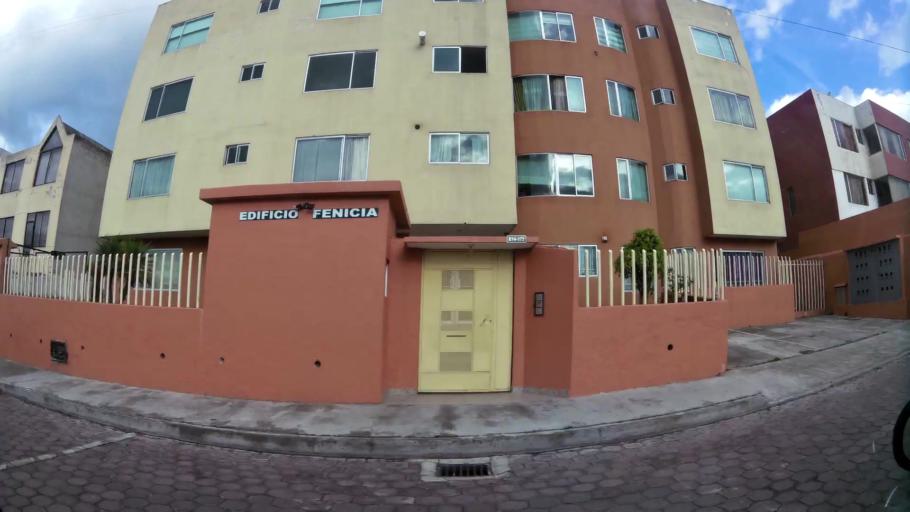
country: EC
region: Pichincha
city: Quito
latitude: -0.1319
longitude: -78.4636
